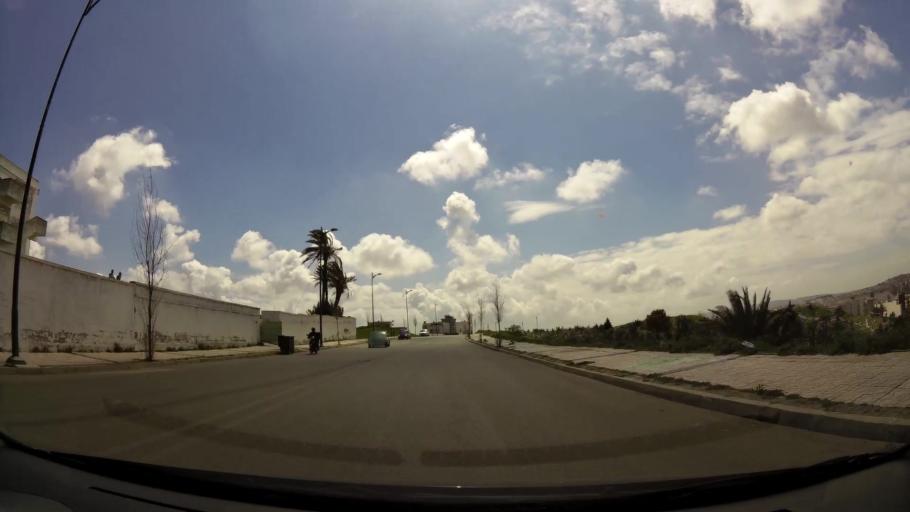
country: MA
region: Tanger-Tetouan
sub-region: Tanger-Assilah
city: Tangier
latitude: 35.7733
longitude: -5.8409
